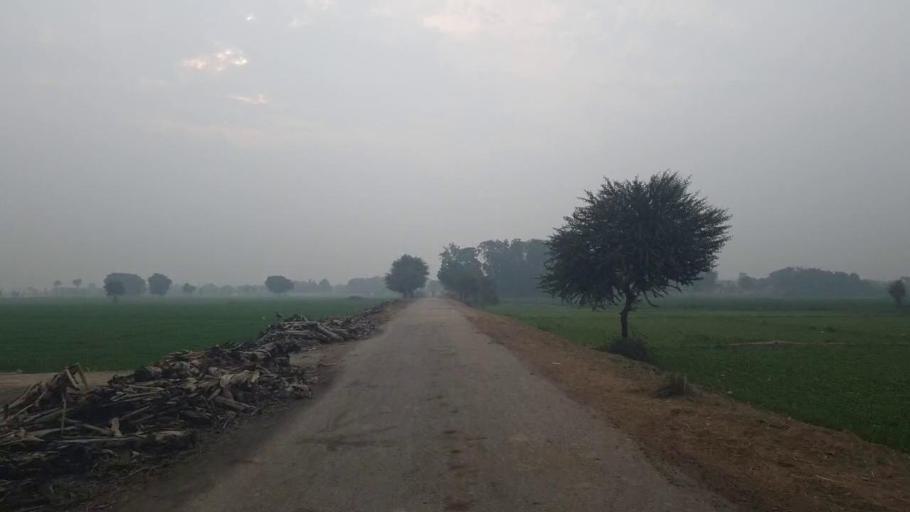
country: PK
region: Sindh
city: Tando Adam
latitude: 25.7343
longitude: 68.6707
